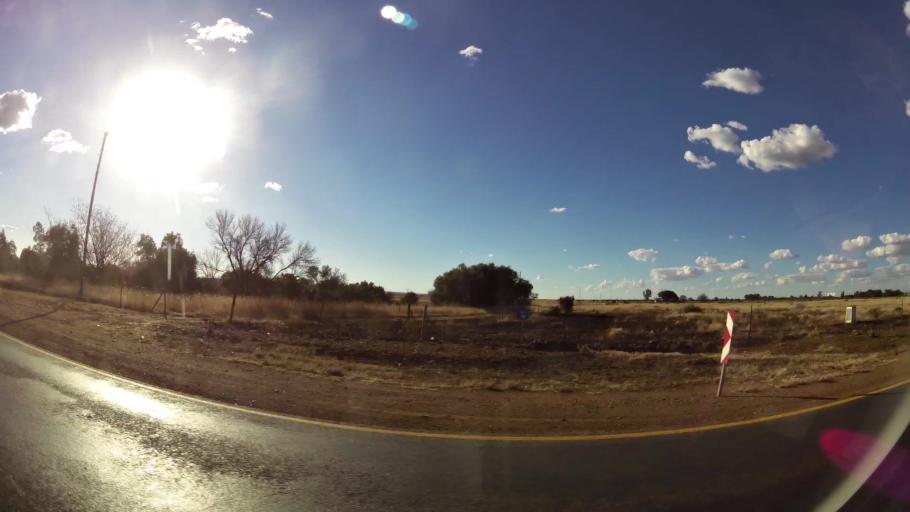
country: ZA
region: North-West
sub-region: Dr Kenneth Kaunda District Municipality
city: Stilfontein
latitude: -26.8425
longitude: 26.7439
